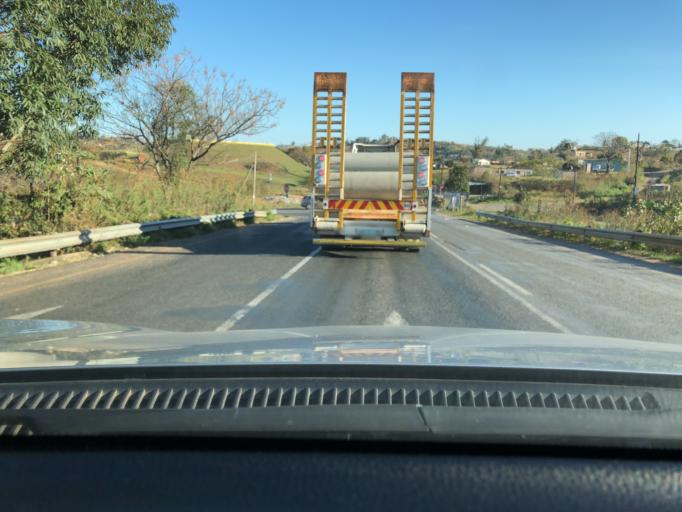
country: ZA
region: KwaZulu-Natal
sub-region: eThekwini Metropolitan Municipality
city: Umkomaas
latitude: -30.0346
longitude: 30.8098
